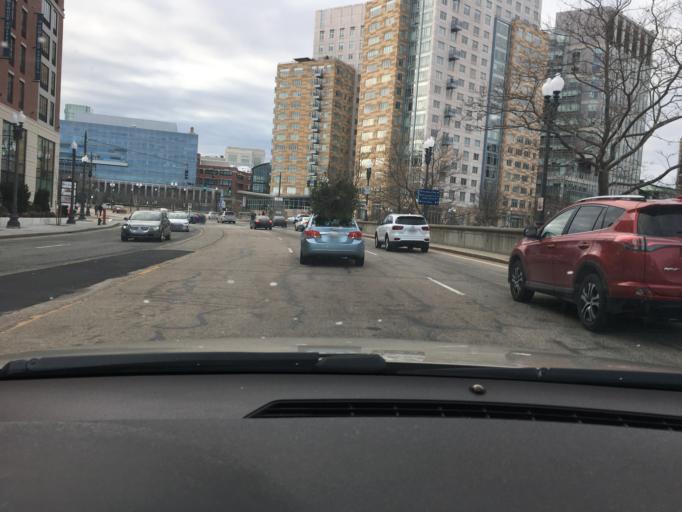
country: US
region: Rhode Island
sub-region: Providence County
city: Providence
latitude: 41.8269
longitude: -71.4111
